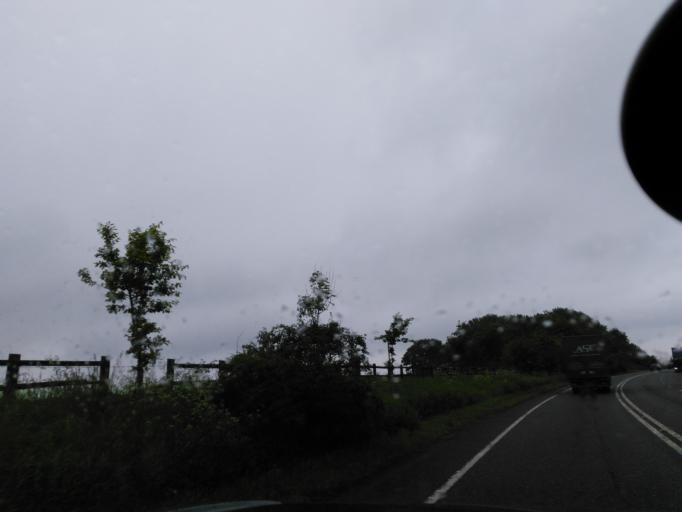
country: GB
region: England
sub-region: Wiltshire
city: Chapmanslade
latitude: 51.2608
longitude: -2.2774
